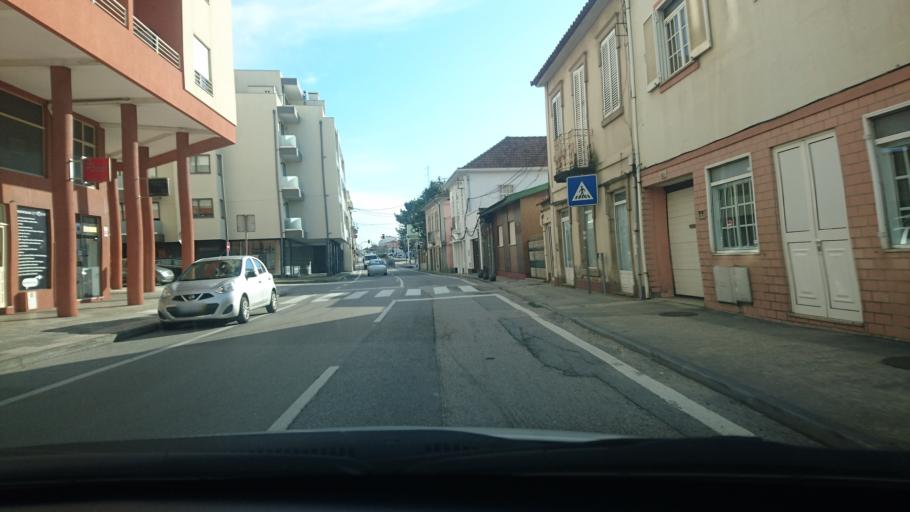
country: PT
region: Aveiro
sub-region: Ovar
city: Esmoriz
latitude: 40.9570
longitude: -8.6266
